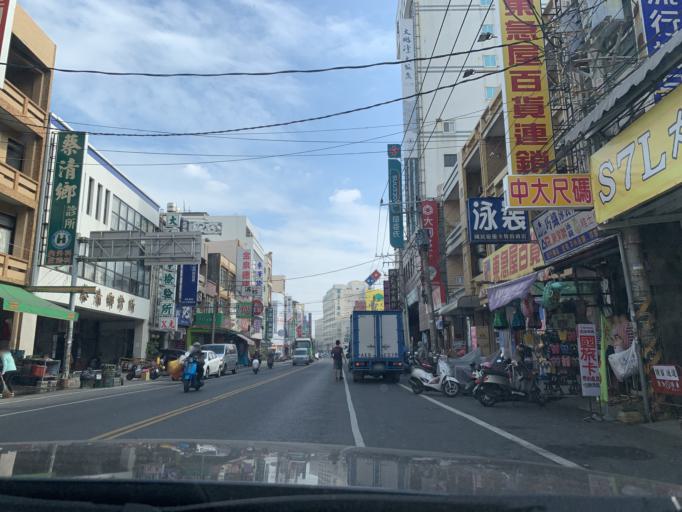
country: TW
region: Taiwan
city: Fengshan
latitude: 22.4667
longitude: 120.4504
